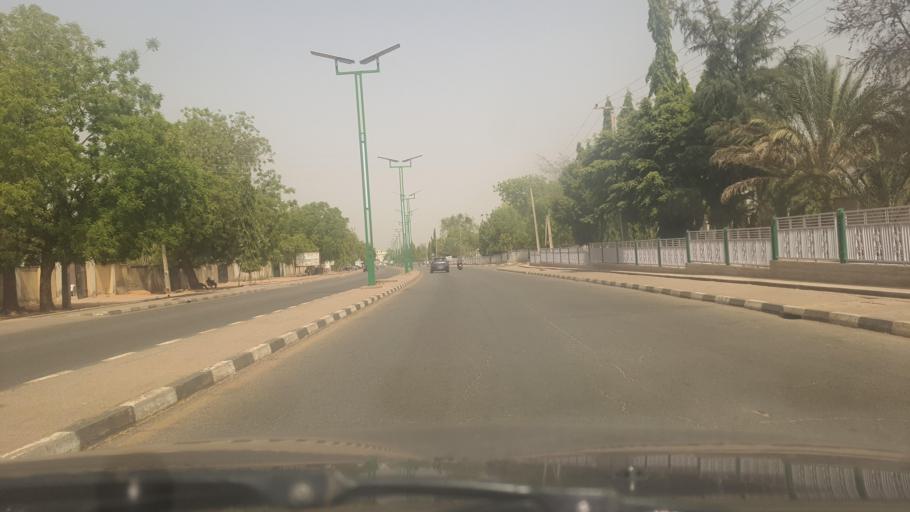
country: NG
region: Gombe
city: Gombe
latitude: 10.2823
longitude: 11.1560
